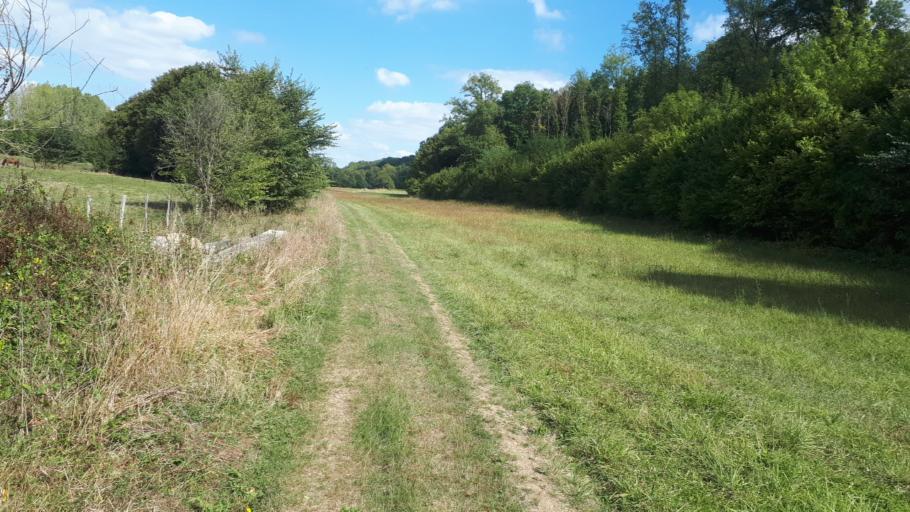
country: FR
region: Centre
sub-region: Departement du Loir-et-Cher
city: Villiers-sur-Loir
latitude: 47.8181
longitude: 0.9654
